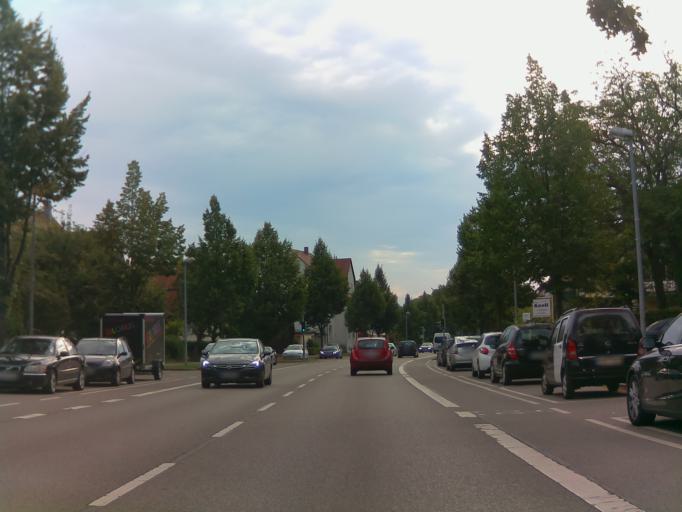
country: DE
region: Baden-Wuerttemberg
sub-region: Regierungsbezirk Stuttgart
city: Leinfelden-Echterdingen
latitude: 48.7300
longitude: 9.1212
